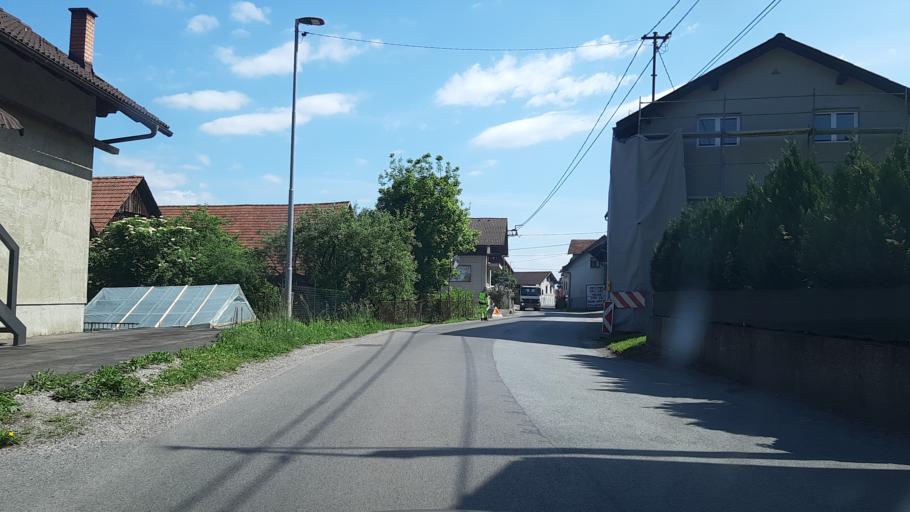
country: SI
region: Brezovica
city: Notranje Gorice
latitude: 45.9723
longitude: 14.4183
